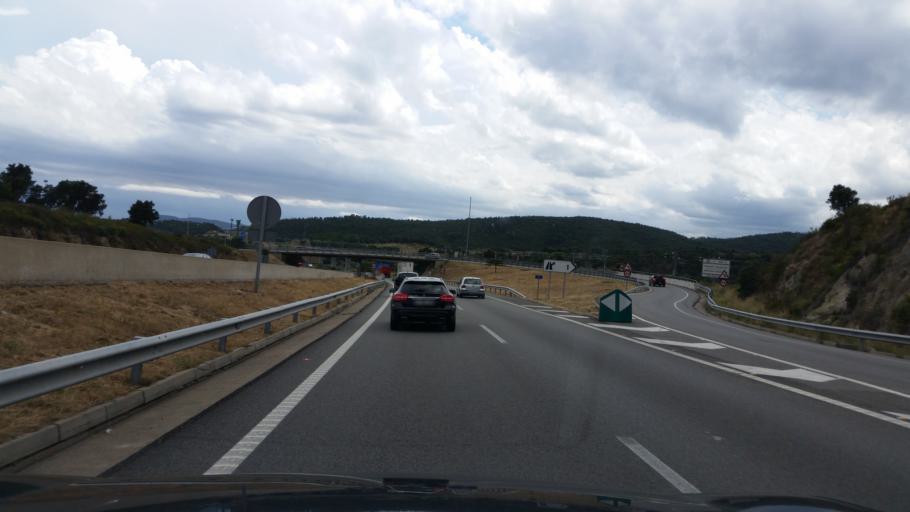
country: ES
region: Catalonia
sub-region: Provincia de Girona
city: la Jonquera
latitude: 42.4346
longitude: 2.8638
